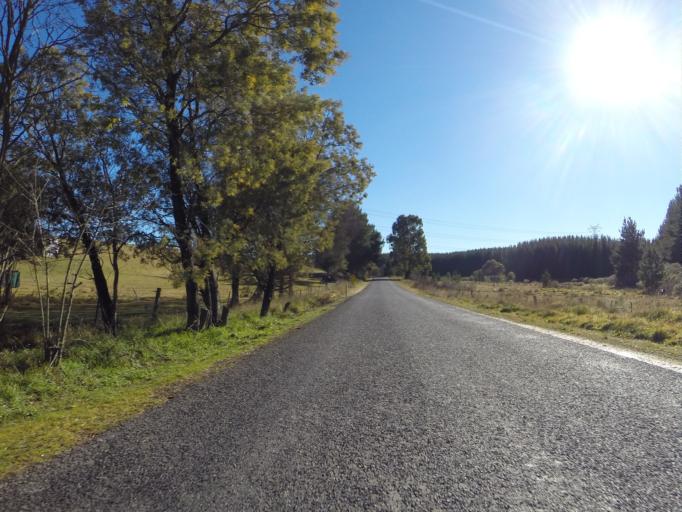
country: AU
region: New South Wales
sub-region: Oberon
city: Oberon
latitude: -33.6536
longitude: 149.8537
